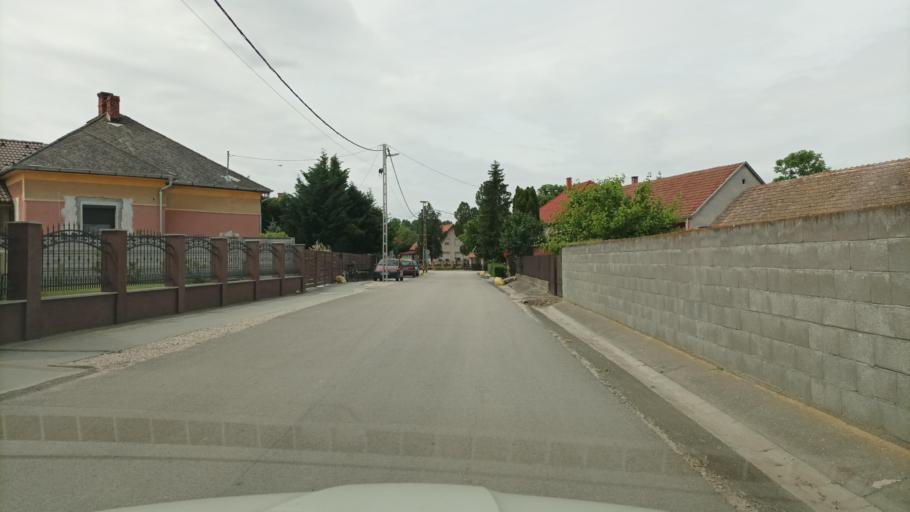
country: HU
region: Fejer
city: Adony
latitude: 47.1142
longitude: 18.8980
